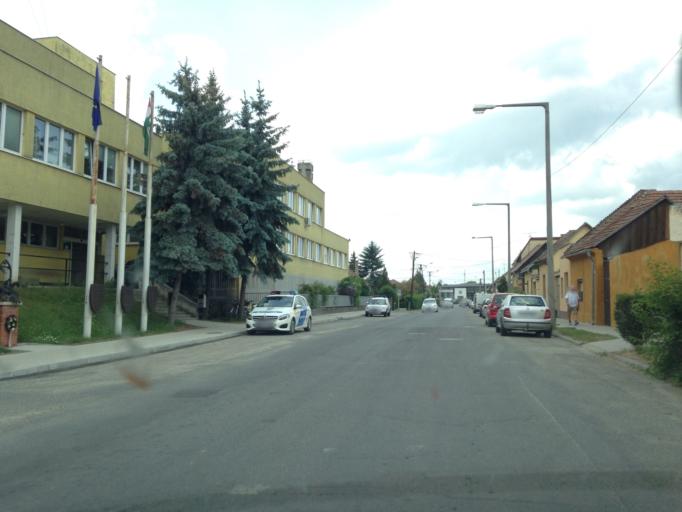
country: HU
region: Komarom-Esztergom
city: Esztergom
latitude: 47.7819
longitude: 18.7396
